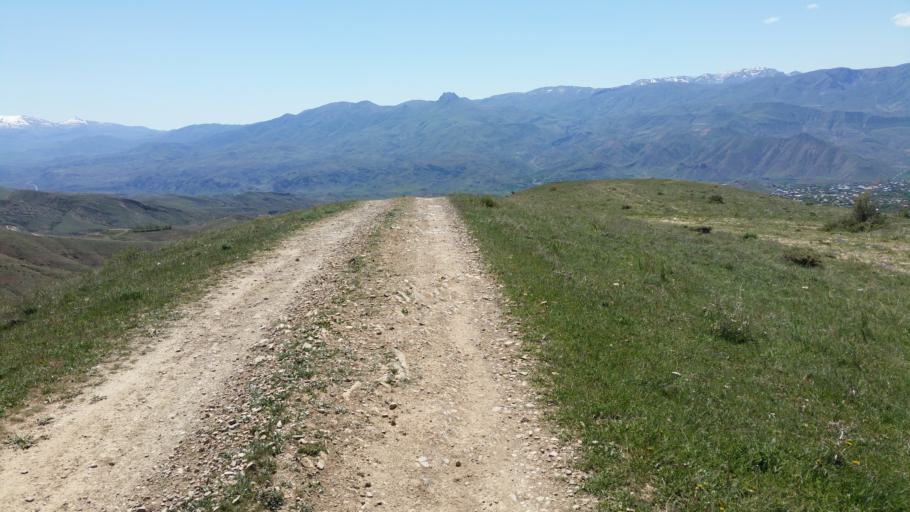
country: AM
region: Vayots' Dzori Marz
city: Vernashen
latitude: 39.8020
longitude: 45.3605
